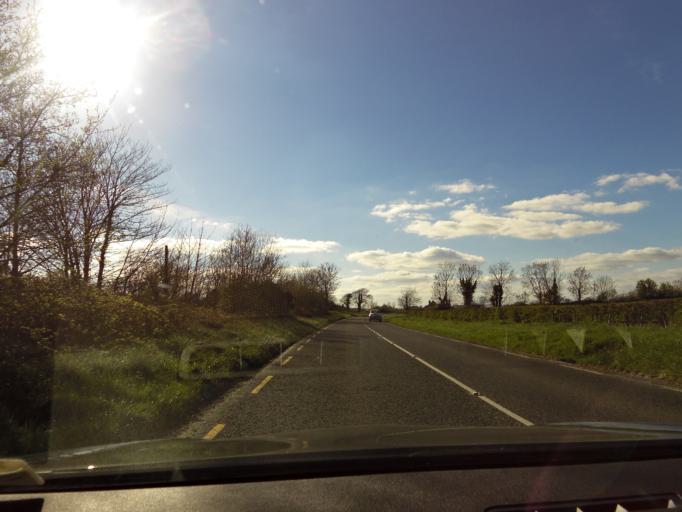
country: IE
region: Leinster
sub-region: Uibh Fhaili
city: Banagher
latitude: 53.1034
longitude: -8.0165
